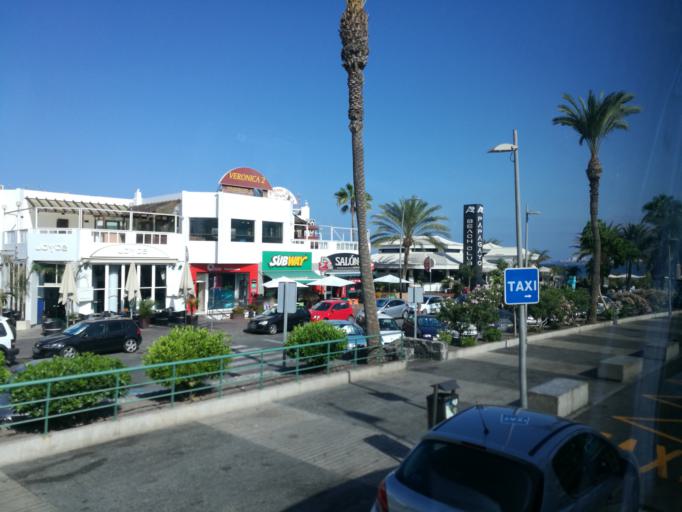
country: ES
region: Canary Islands
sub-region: Provincia de Santa Cruz de Tenerife
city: Playa de las Americas
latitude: 28.0660
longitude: -16.7320
